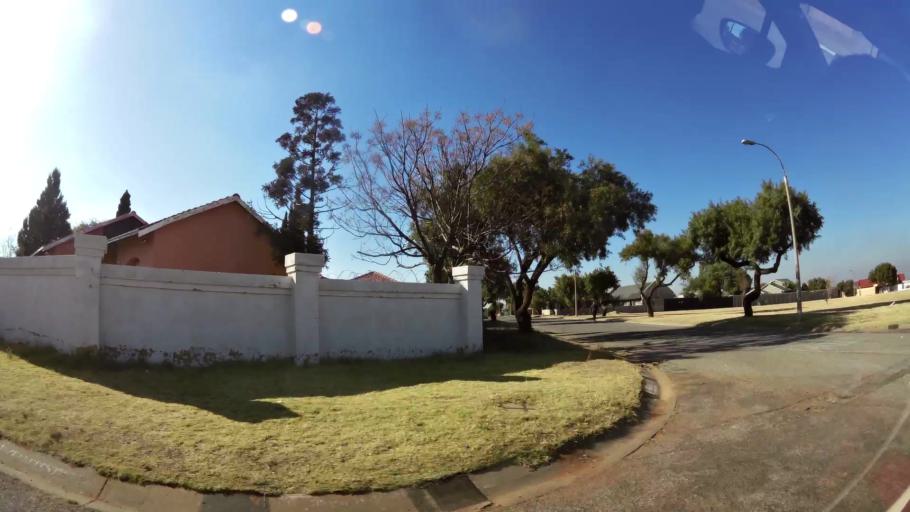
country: ZA
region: Gauteng
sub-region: City of Johannesburg Metropolitan Municipality
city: Roodepoort
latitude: -26.1625
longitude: 27.8190
